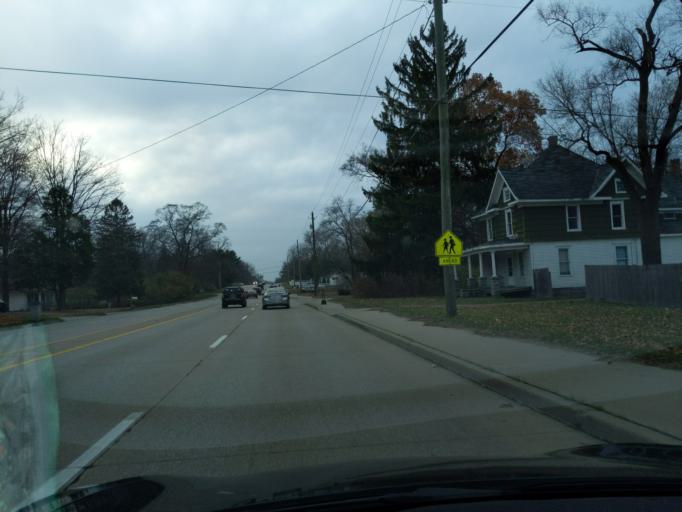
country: US
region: Indiana
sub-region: Saint Joseph County
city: Georgetown
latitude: 41.7232
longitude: -86.2400
